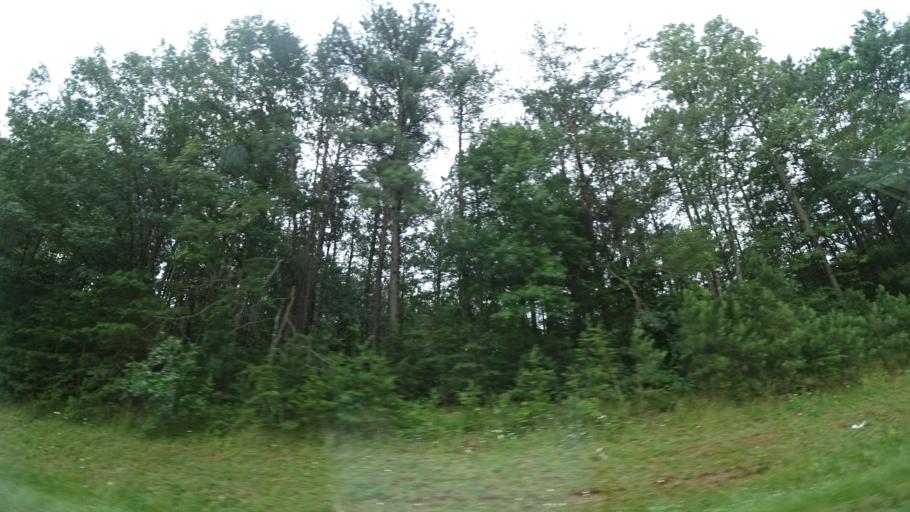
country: US
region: Virginia
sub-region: Spotsylvania County
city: Spotsylvania Courthouse
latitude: 38.1474
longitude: -77.7003
